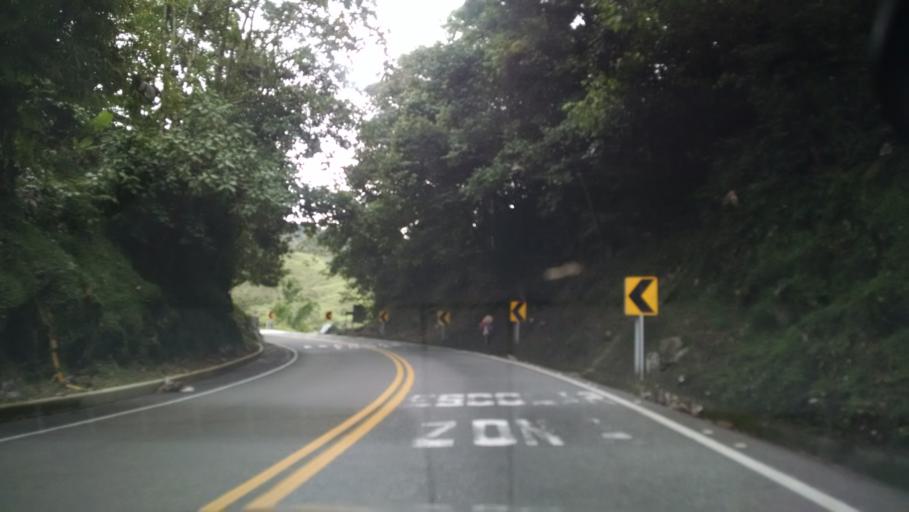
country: CO
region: Antioquia
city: Cocorna
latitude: 6.0253
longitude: -75.1680
